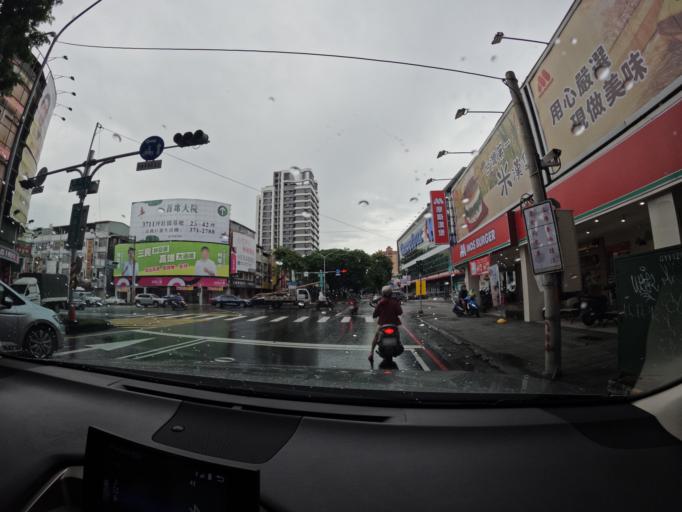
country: TW
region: Kaohsiung
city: Kaohsiung
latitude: 22.6536
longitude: 120.3187
